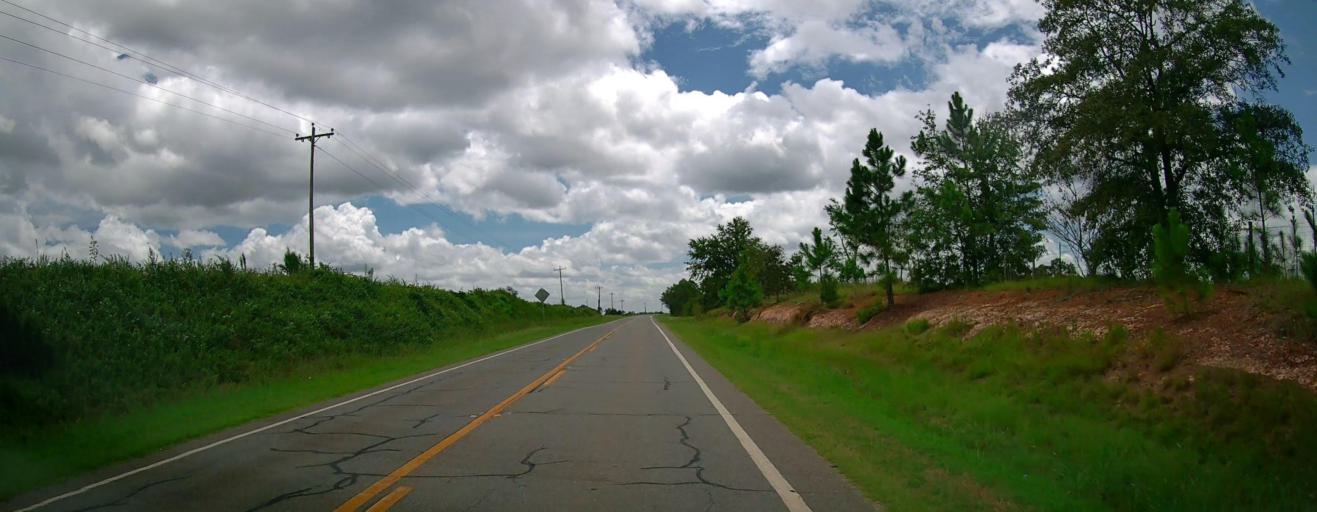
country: US
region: Georgia
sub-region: Wilcox County
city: Rochelle
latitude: 31.9870
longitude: -83.5454
